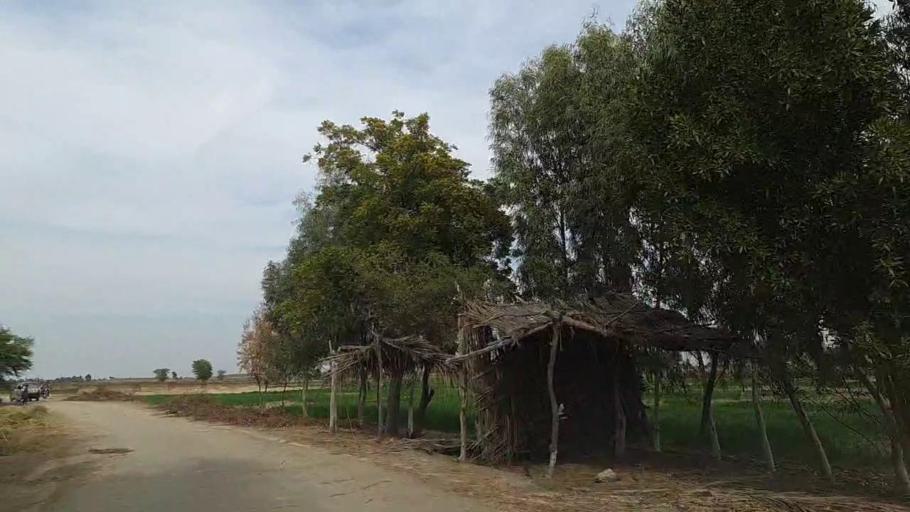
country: PK
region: Sindh
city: Jam Sahib
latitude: 26.4001
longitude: 68.5404
